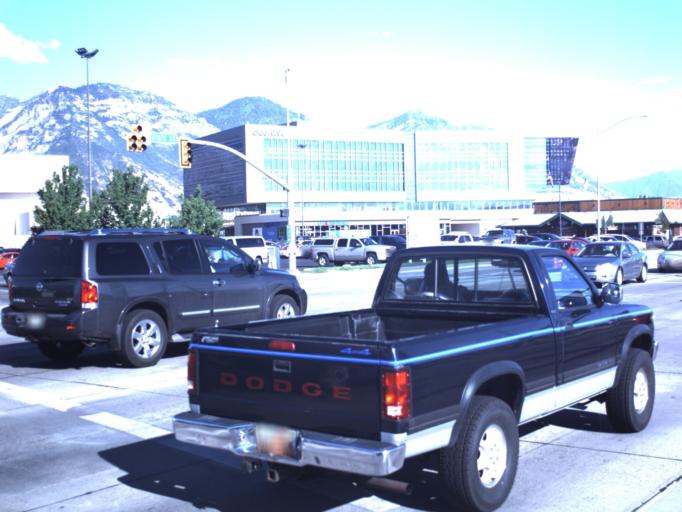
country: US
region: Utah
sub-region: Utah County
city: Orem
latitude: 40.2753
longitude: -111.6855
